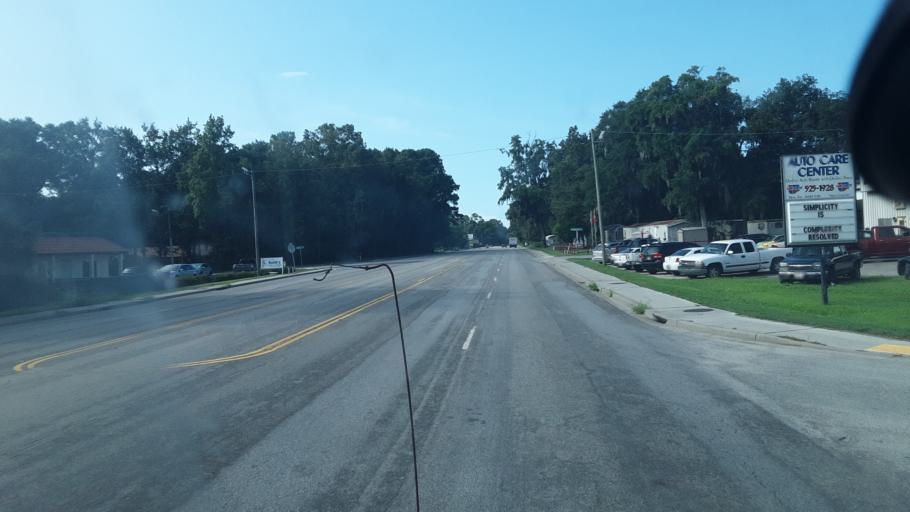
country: US
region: South Carolina
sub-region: Beaufort County
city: Shell Point
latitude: 32.4070
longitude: -80.7343
